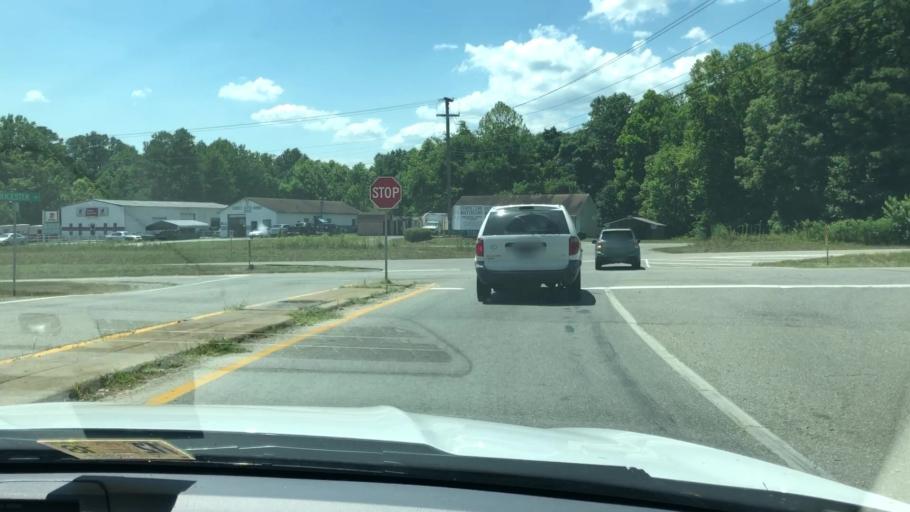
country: US
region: Virginia
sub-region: Middlesex County
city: Saluda
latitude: 37.5967
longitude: -76.6033
